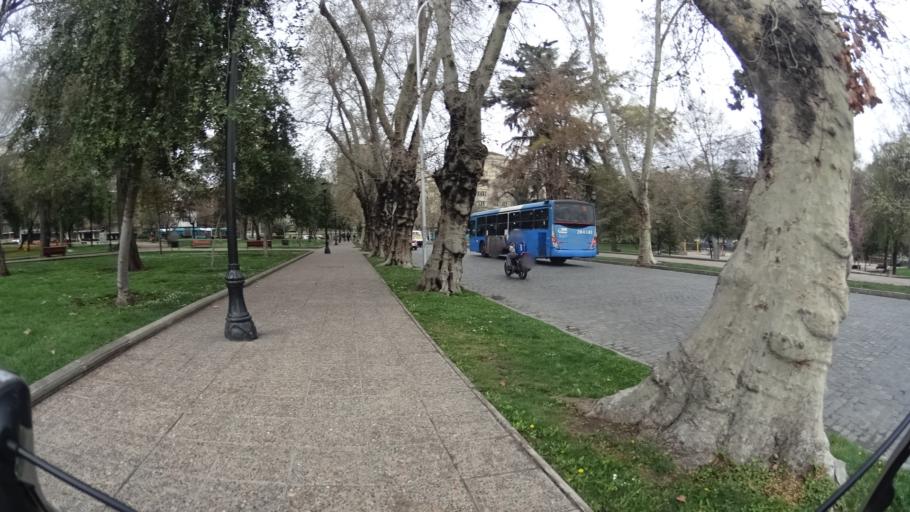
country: CL
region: Santiago Metropolitan
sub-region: Provincia de Santiago
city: Santiago
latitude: -33.4359
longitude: -70.6389
